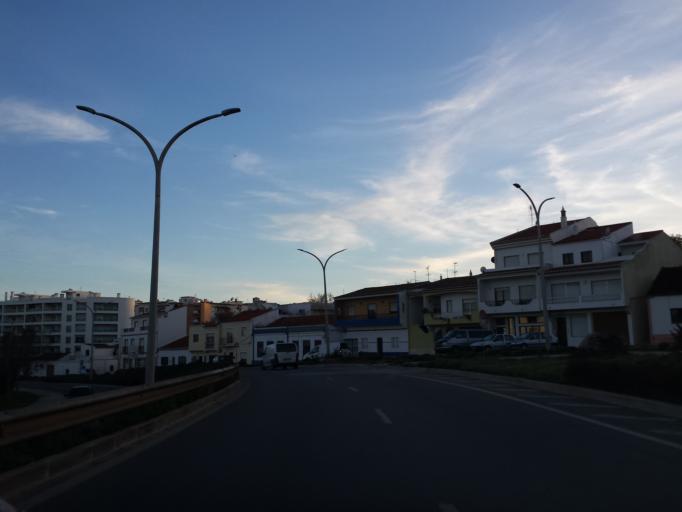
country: PT
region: Faro
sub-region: Lagos
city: Lagos
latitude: 37.1130
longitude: -8.6815
